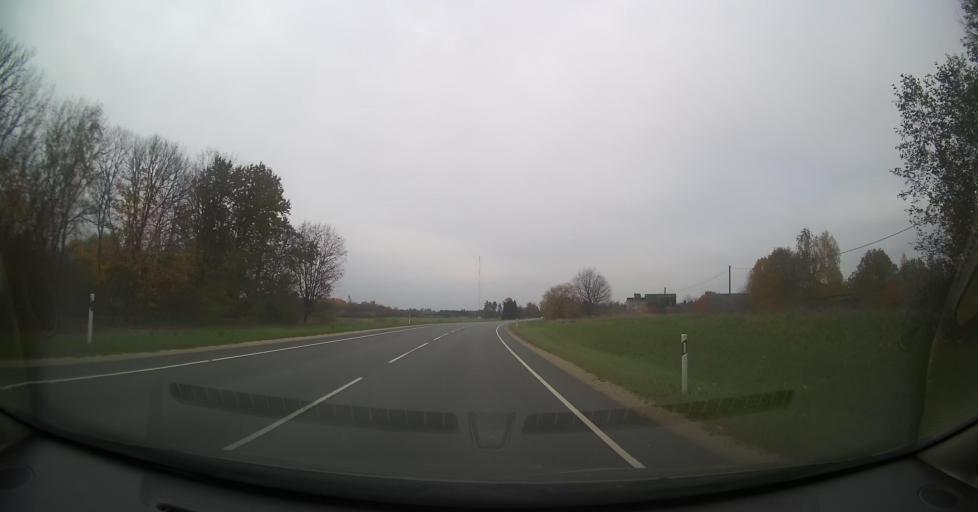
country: EE
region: Harju
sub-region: Nissi vald
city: Turba
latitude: 59.0382
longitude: 24.1675
